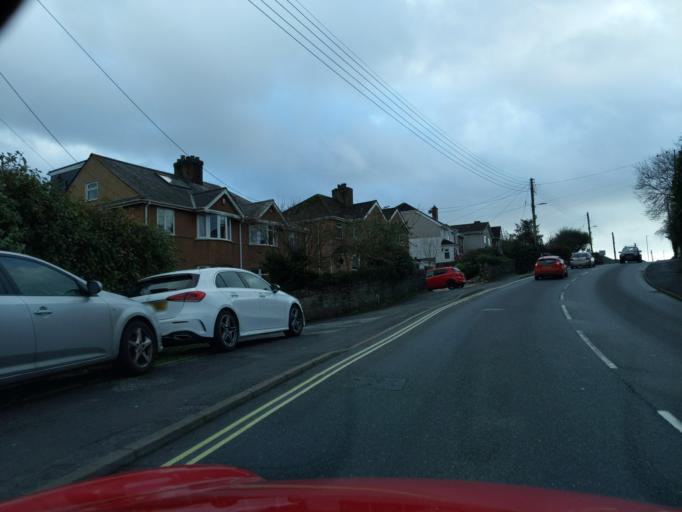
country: GB
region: England
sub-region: Plymouth
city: Plymstock
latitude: 50.3634
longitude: -4.0653
